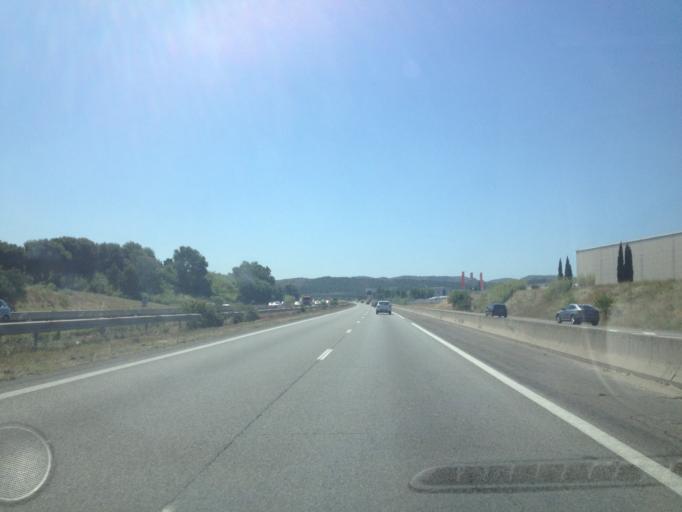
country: FR
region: Provence-Alpes-Cote d'Azur
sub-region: Departement des Bouches-du-Rhone
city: Saint-Victoret
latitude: 43.4266
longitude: 5.2629
